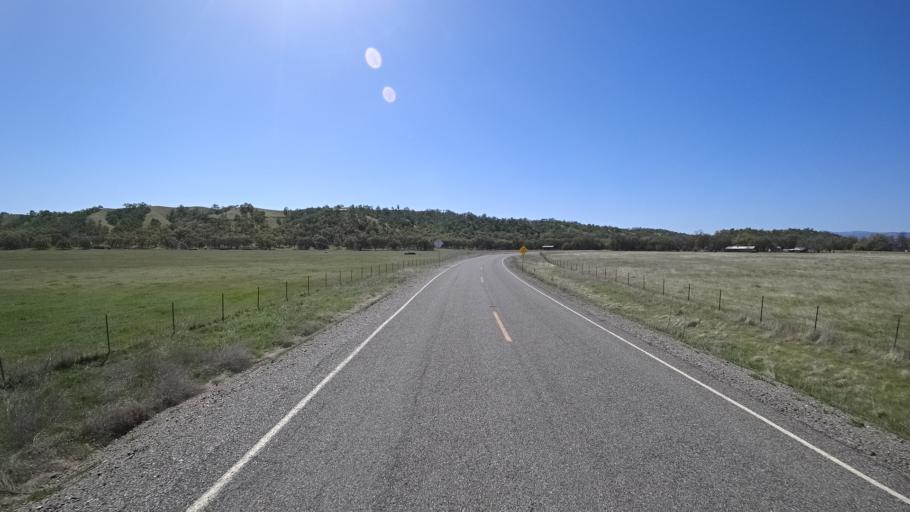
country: US
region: California
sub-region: Tehama County
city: Rancho Tehama Reserve
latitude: 39.8037
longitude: -122.4260
